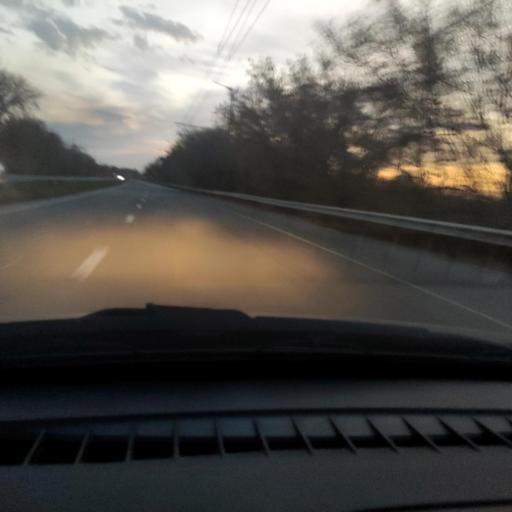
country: RU
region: Samara
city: Zhigulevsk
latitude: 53.5390
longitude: 49.5662
